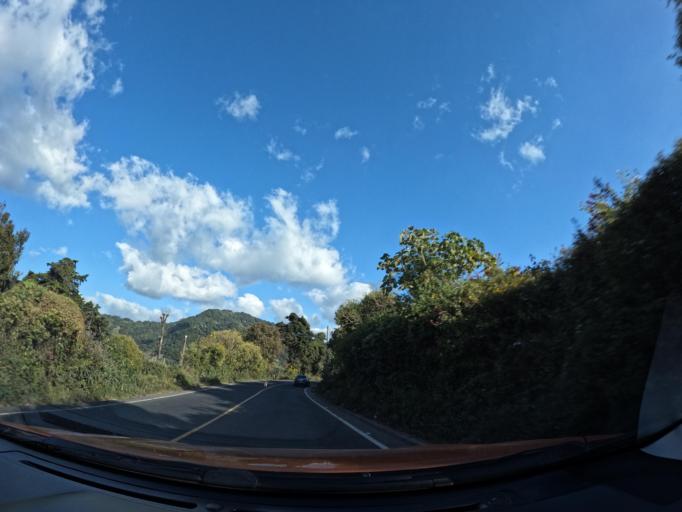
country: GT
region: Sacatepequez
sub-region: Municipio de Santa Maria de Jesus
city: Santa Maria de Jesus
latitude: 14.4841
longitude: -90.7036
